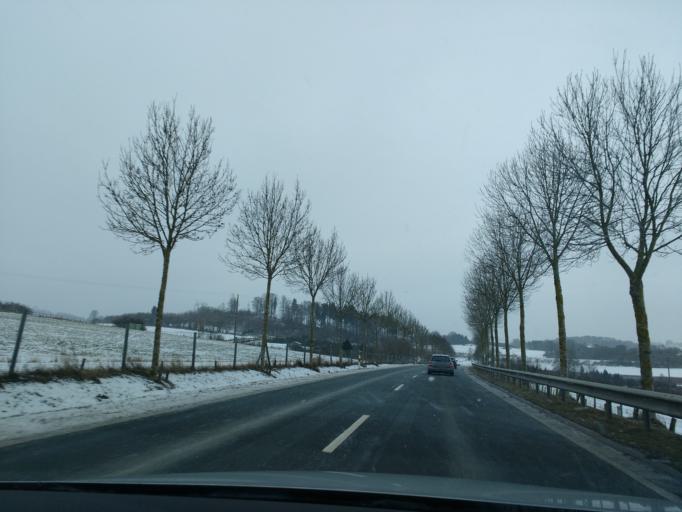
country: DE
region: North Rhine-Westphalia
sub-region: Regierungsbezirk Arnsberg
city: Brilon
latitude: 51.3997
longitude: 8.5992
